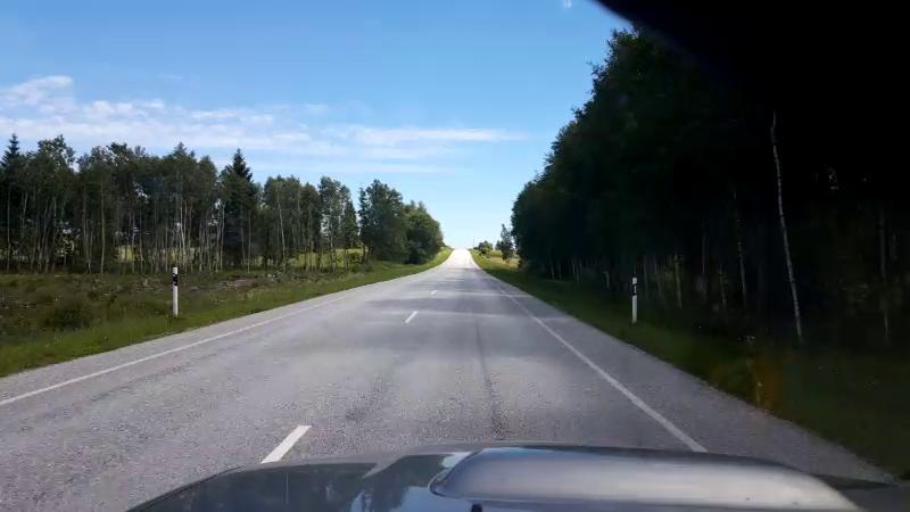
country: EE
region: Jaervamaa
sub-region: Koeru vald
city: Koeru
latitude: 58.9685
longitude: 26.1391
